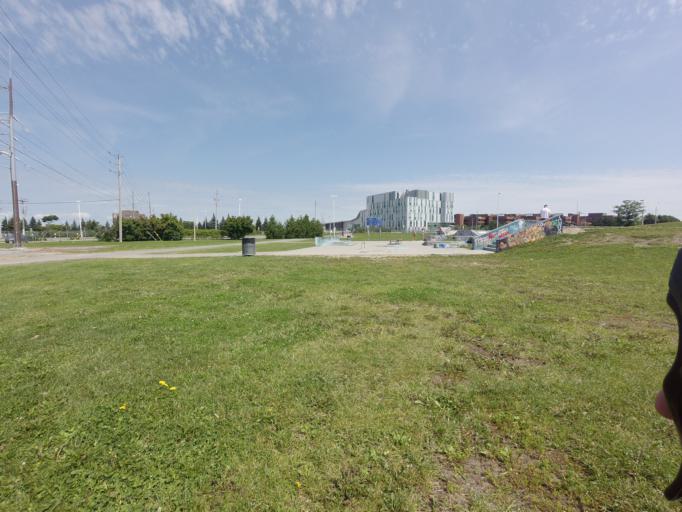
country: CA
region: Ontario
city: Bells Corners
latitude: 45.3454
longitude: -75.7613
